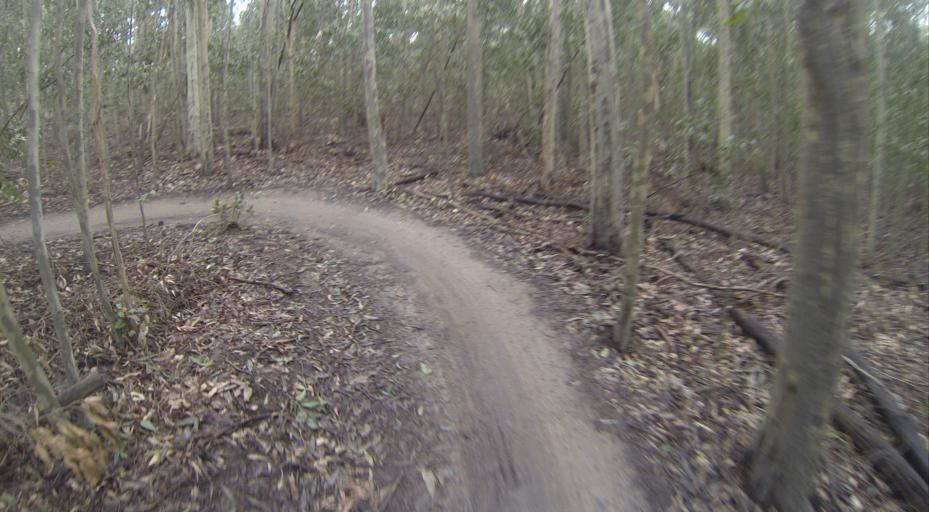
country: AU
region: Victoria
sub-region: Yarra Ranges
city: Lysterfield
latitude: -37.9424
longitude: 145.3024
